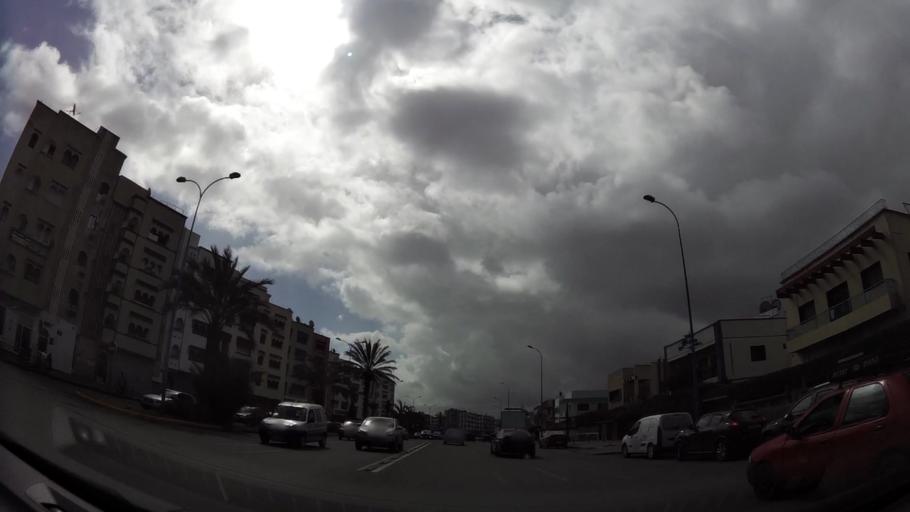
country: MA
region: Grand Casablanca
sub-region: Casablanca
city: Casablanca
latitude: 33.5528
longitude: -7.6039
